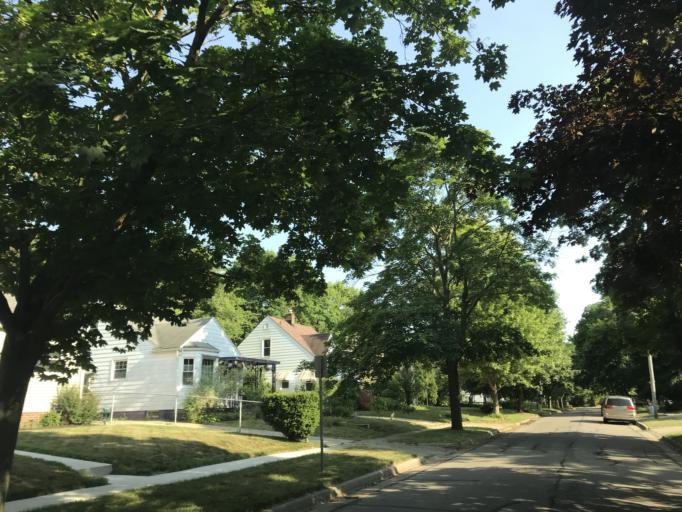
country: US
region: Michigan
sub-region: Washtenaw County
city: Ypsilanti
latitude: 42.2516
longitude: -83.6055
